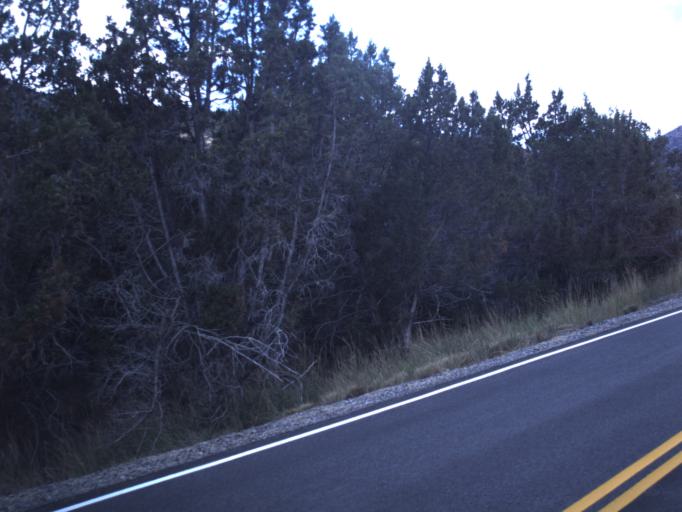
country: US
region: Utah
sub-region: Tooele County
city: Grantsville
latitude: 40.3386
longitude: -112.5350
